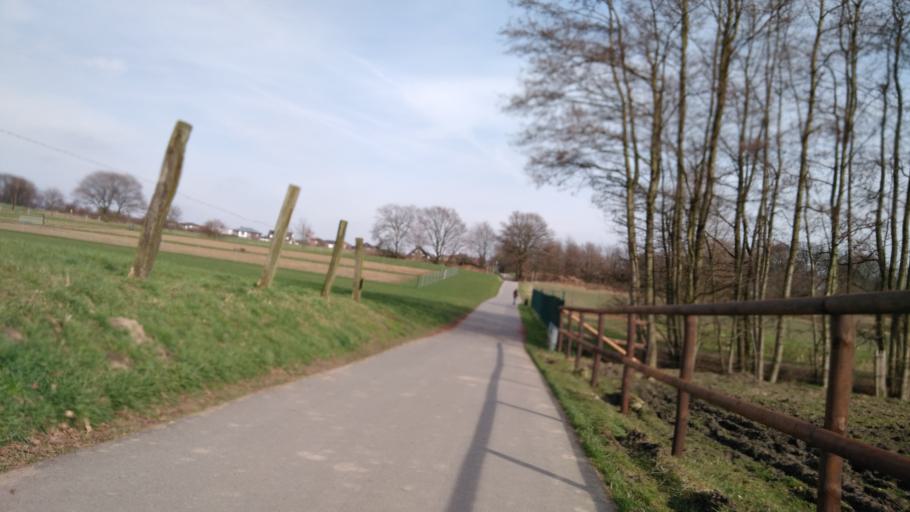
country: DE
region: North Rhine-Westphalia
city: Herten
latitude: 51.6085
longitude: 7.1585
